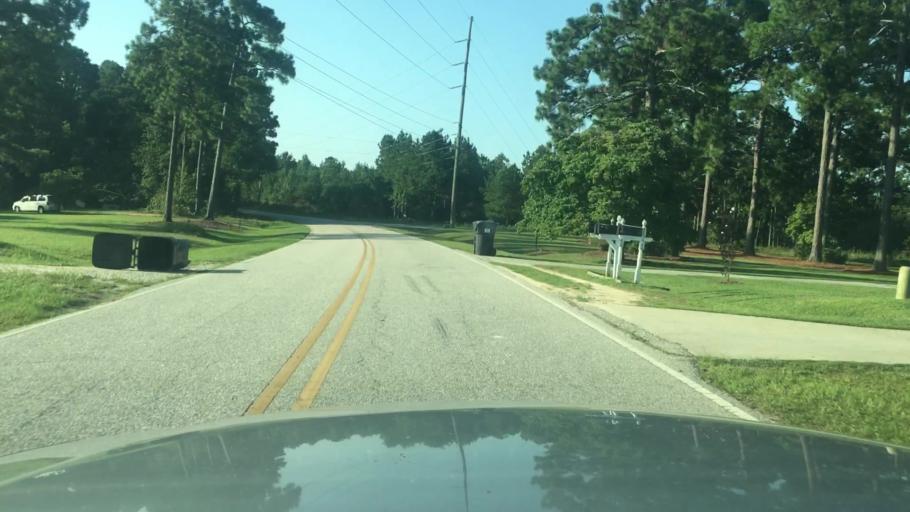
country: US
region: North Carolina
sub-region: Cumberland County
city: Spring Lake
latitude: 35.2117
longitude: -78.8956
